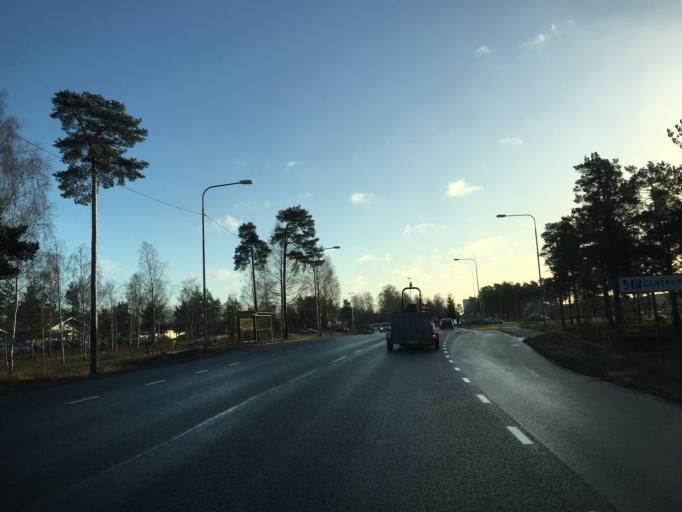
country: SE
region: Kalmar
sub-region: Vasterviks Kommun
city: Vaestervik
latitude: 57.7661
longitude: 16.5982
